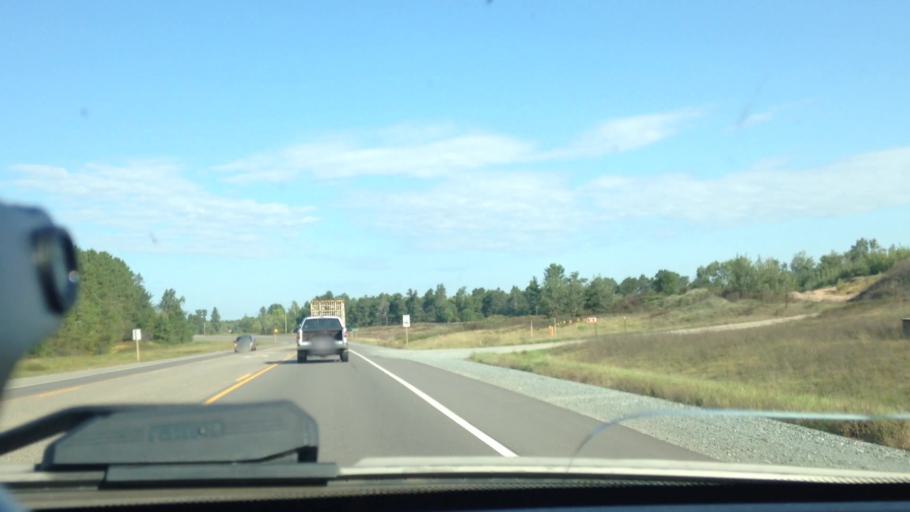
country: US
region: Michigan
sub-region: Dickinson County
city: Iron Mountain
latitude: 45.8718
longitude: -88.0837
